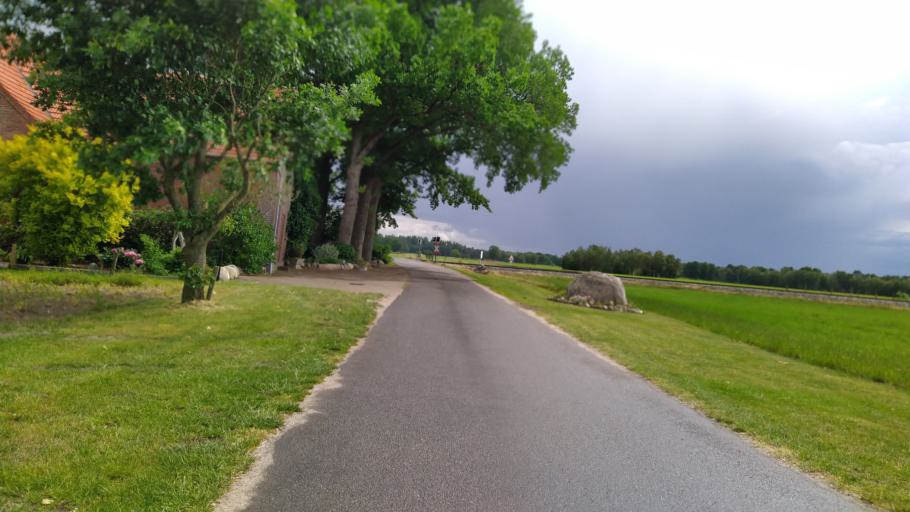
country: DE
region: Lower Saxony
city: Kutenholz
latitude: 53.4669
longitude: 9.3440
